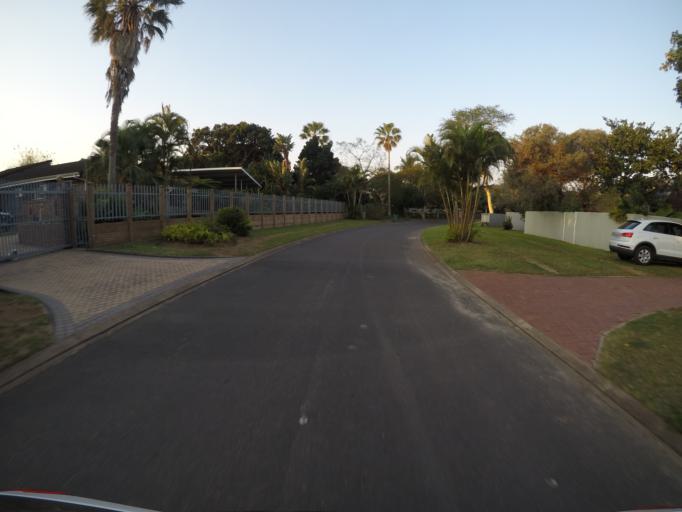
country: ZA
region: KwaZulu-Natal
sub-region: uThungulu District Municipality
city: Richards Bay
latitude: -28.7678
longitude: 32.1161
